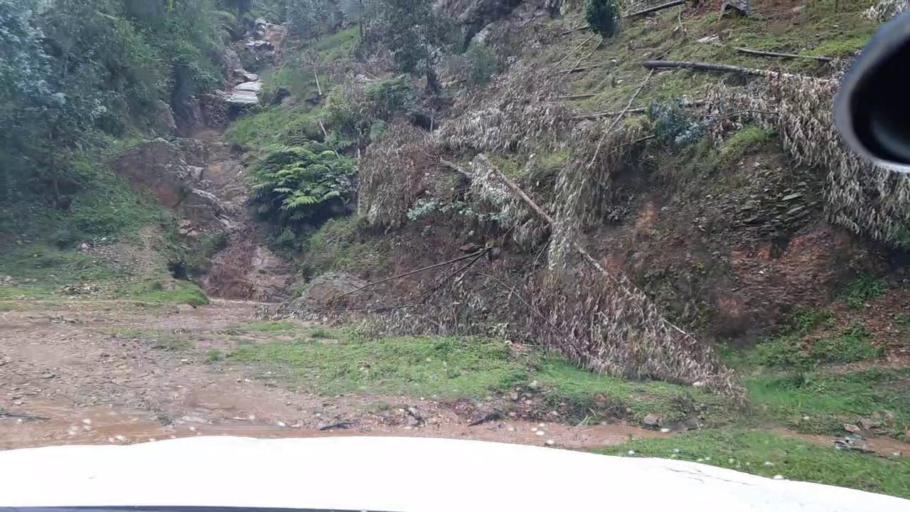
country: RW
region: Western Province
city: Kibuye
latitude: -2.1358
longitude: 29.4571
